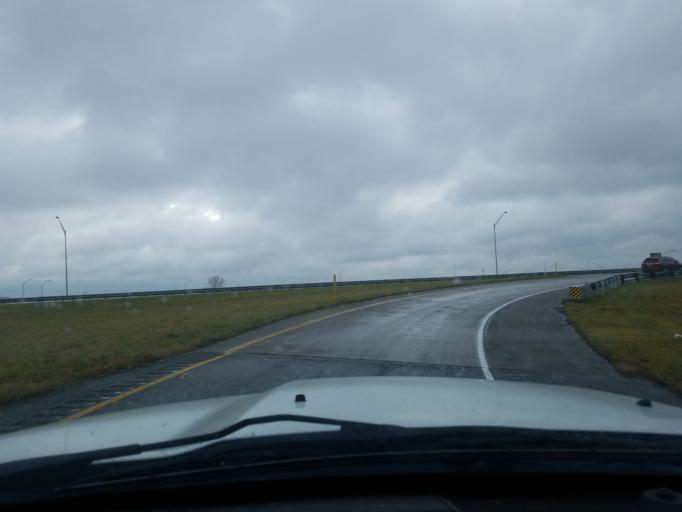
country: US
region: Indiana
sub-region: Clark County
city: Clarksville
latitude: 38.3464
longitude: -85.7525
